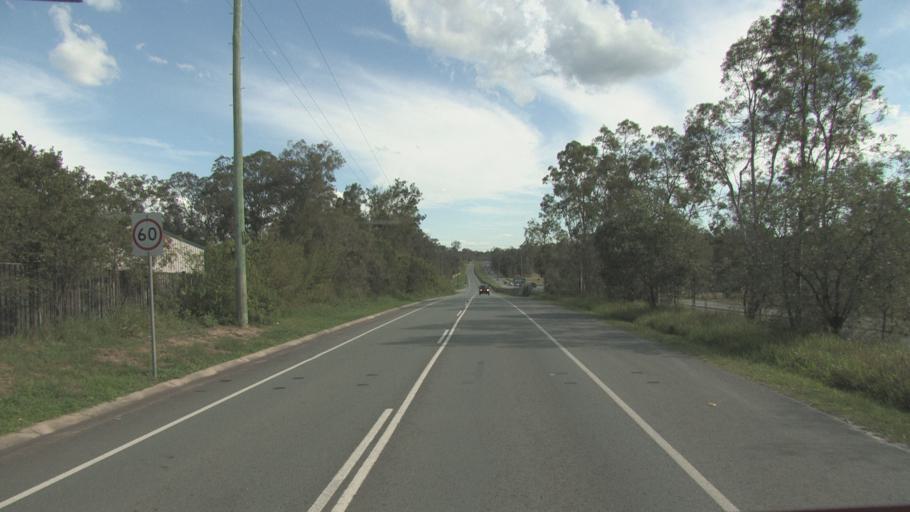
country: AU
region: Queensland
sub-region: Logan
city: Park Ridge South
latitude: -27.7274
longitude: 153.0301
